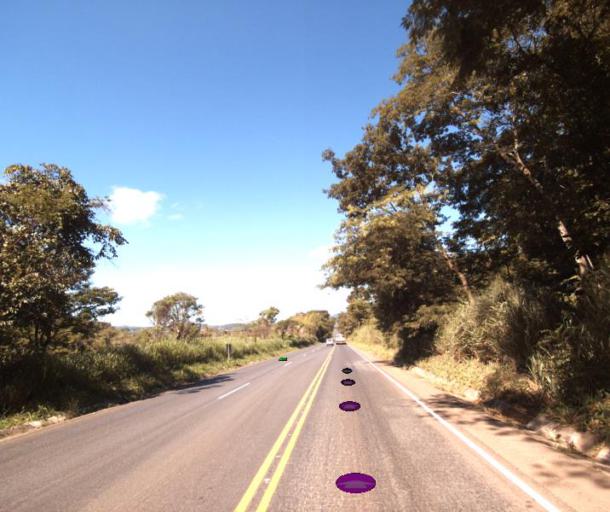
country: BR
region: Goias
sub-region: Ceres
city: Ceres
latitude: -15.1523
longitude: -49.5367
